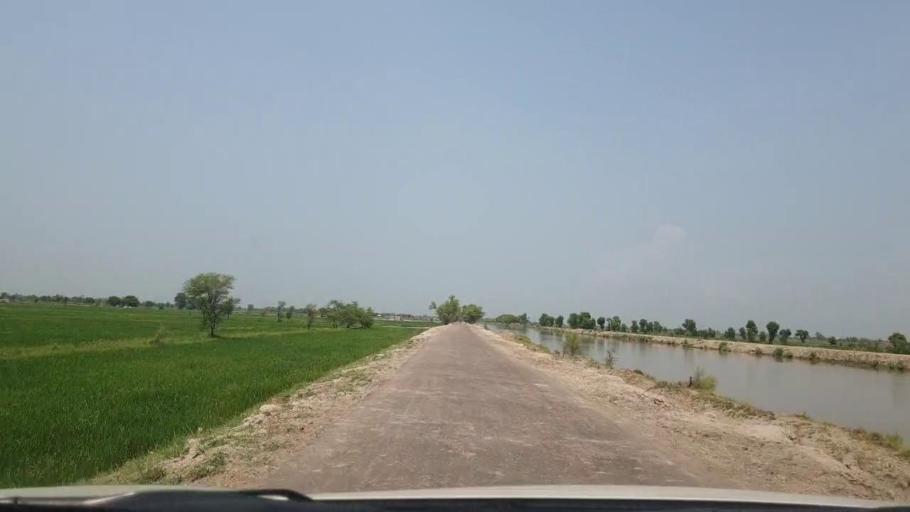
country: PK
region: Sindh
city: Dokri
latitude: 27.3405
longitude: 68.1109
